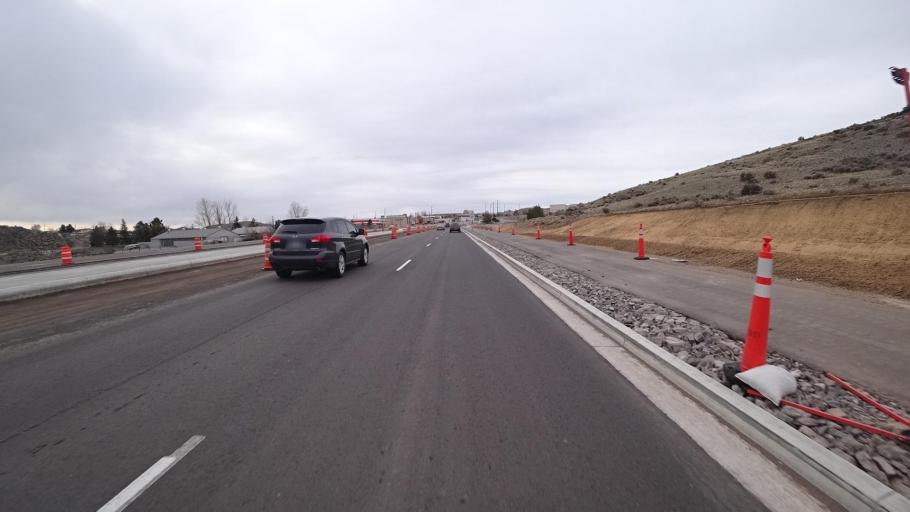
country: US
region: Nevada
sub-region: Washoe County
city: Lemmon Valley
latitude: 39.6178
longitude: -119.8486
